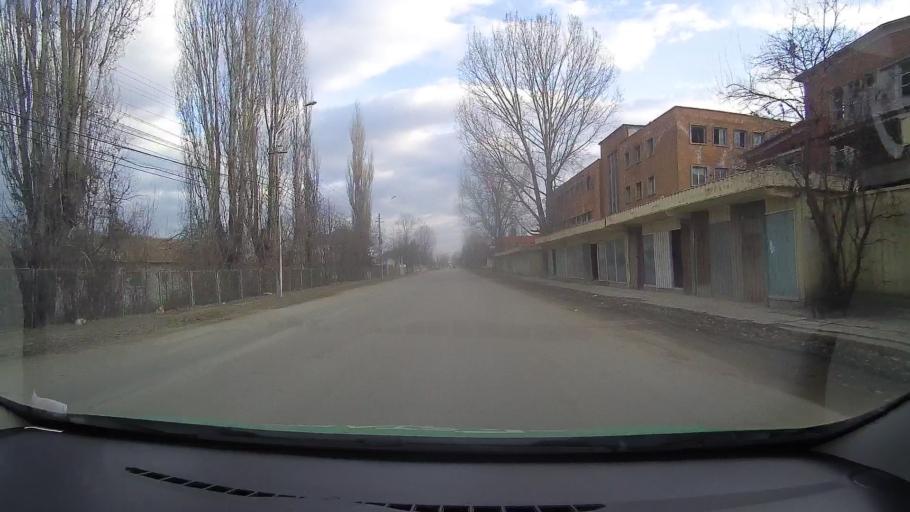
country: RO
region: Dambovita
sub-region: Municipiul Moreni
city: Moreni
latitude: 44.9704
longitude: 25.6514
